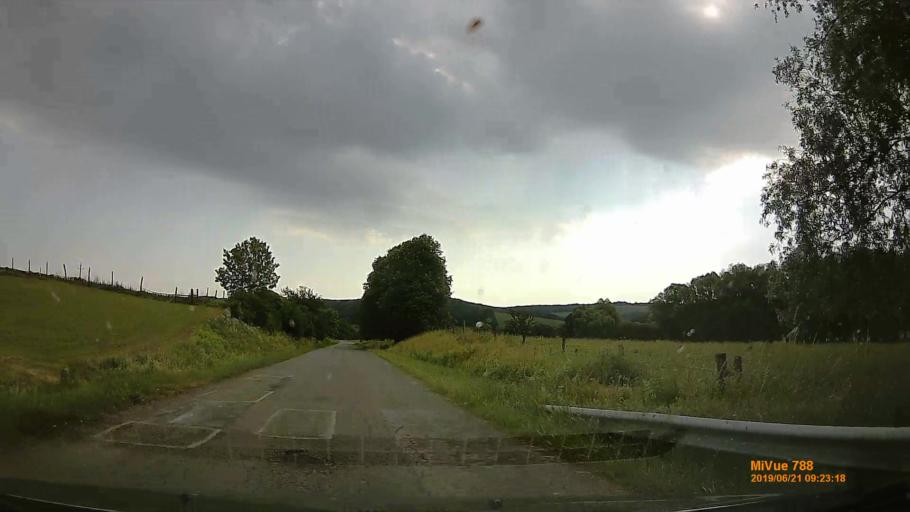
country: HU
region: Somogy
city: Taszar
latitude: 46.2501
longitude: 17.8961
